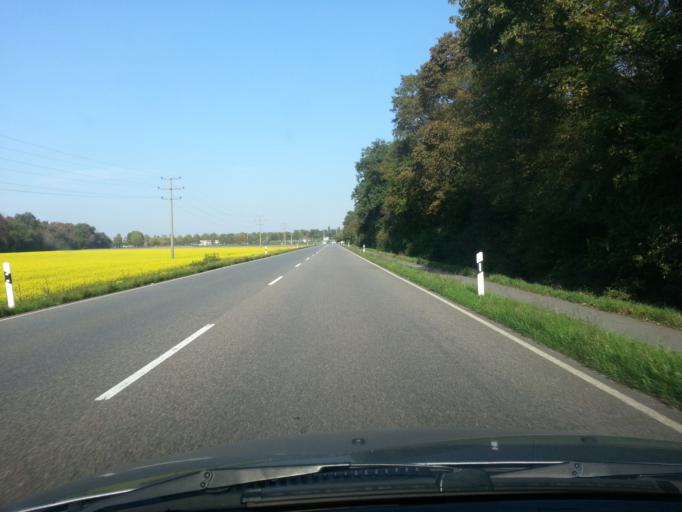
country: DE
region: Baden-Wuerttemberg
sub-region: Karlsruhe Region
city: Ketsch
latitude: 49.3709
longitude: 8.5565
